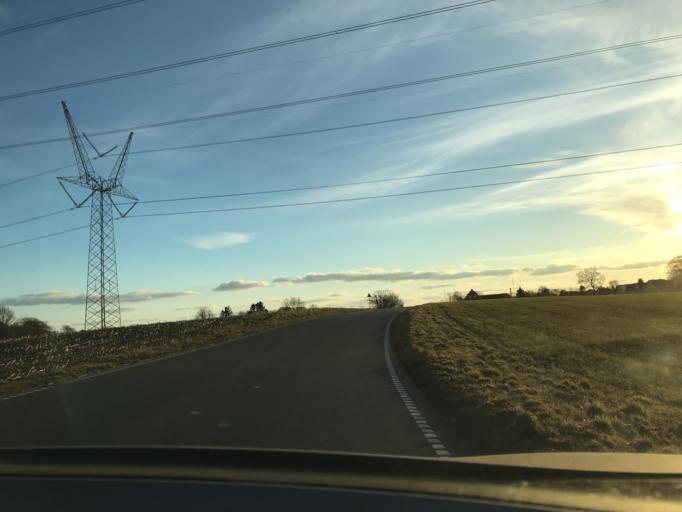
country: DK
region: South Denmark
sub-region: Middelfart Kommune
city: Norre Aby
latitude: 55.4569
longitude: 9.8467
